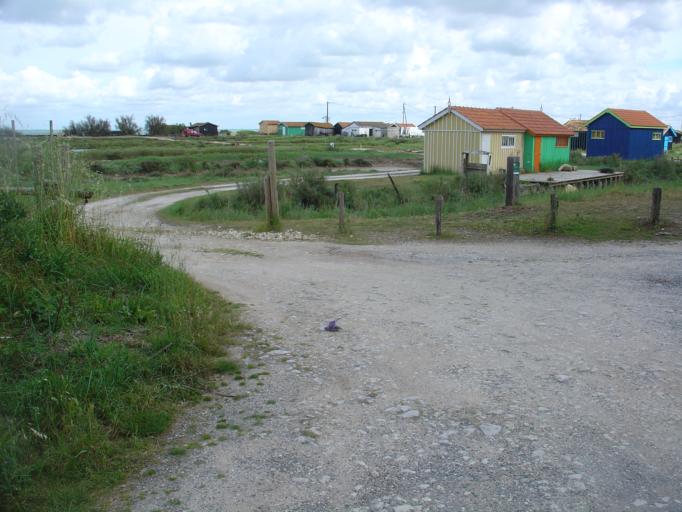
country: FR
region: Poitou-Charentes
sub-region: Departement de la Charente-Maritime
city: Boyard-Ville
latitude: 45.9608
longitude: -1.2435
